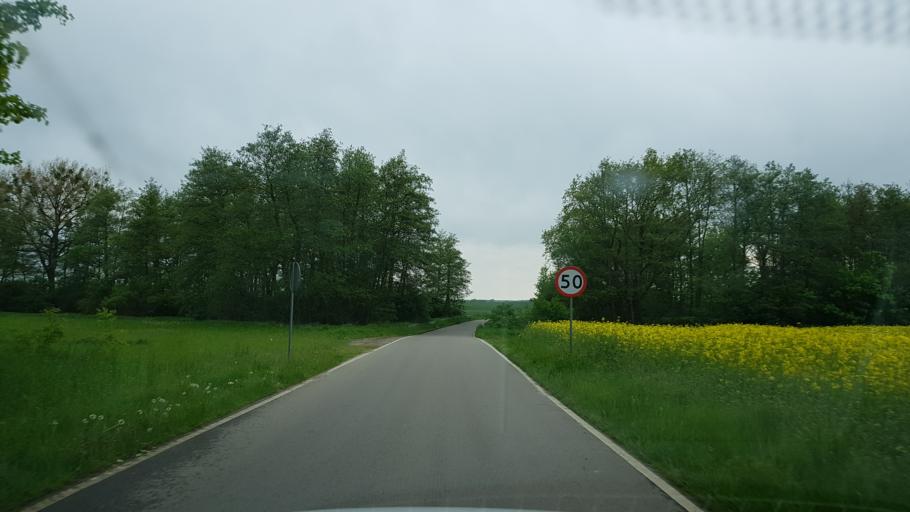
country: PL
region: West Pomeranian Voivodeship
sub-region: Powiat pyrzycki
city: Kozielice
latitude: 53.1222
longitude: 14.7565
